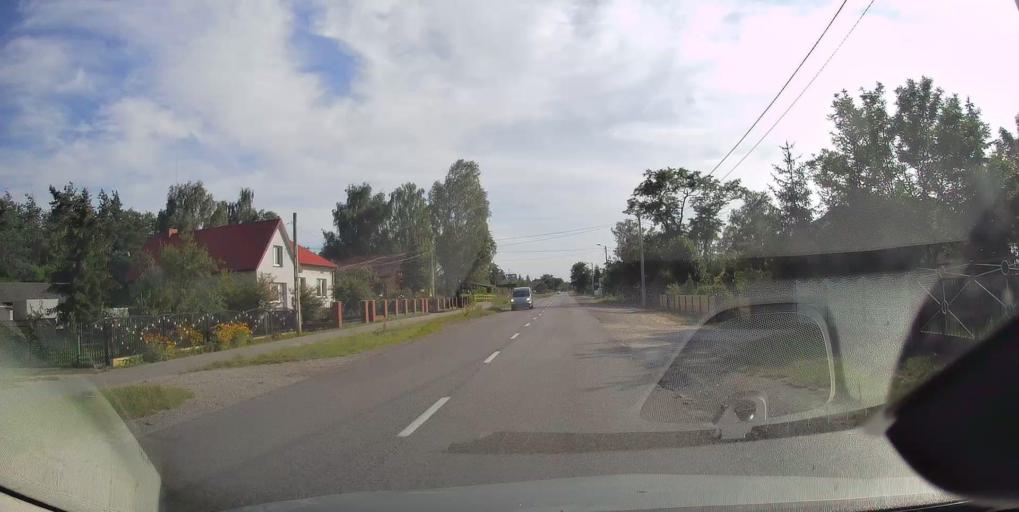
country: PL
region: Swietokrzyskie
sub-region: Powiat konecki
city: Radoszyce
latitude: 51.0785
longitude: 20.2822
